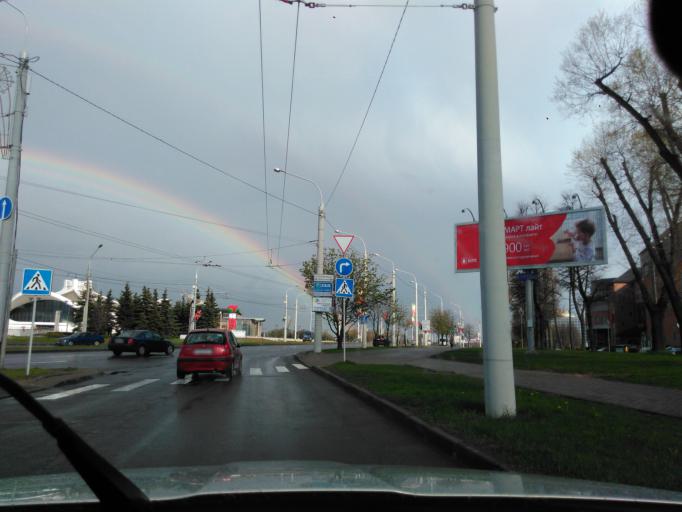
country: BY
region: Minsk
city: Minsk
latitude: 53.9279
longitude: 27.5163
